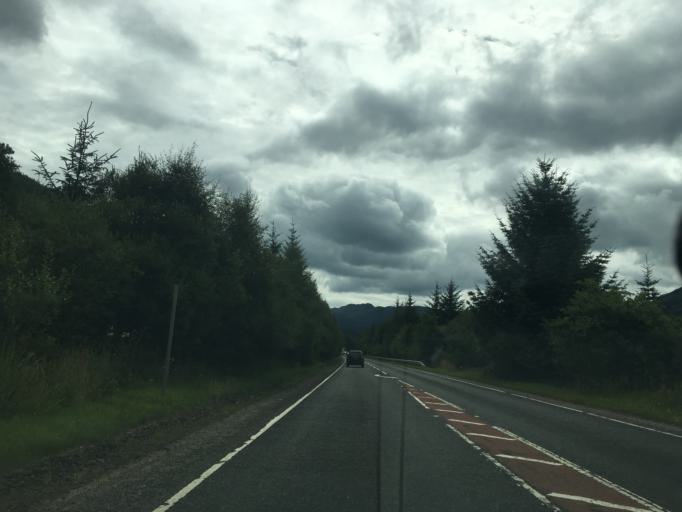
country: GB
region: Scotland
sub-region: Stirling
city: Callander
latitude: 56.3494
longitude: -4.3283
